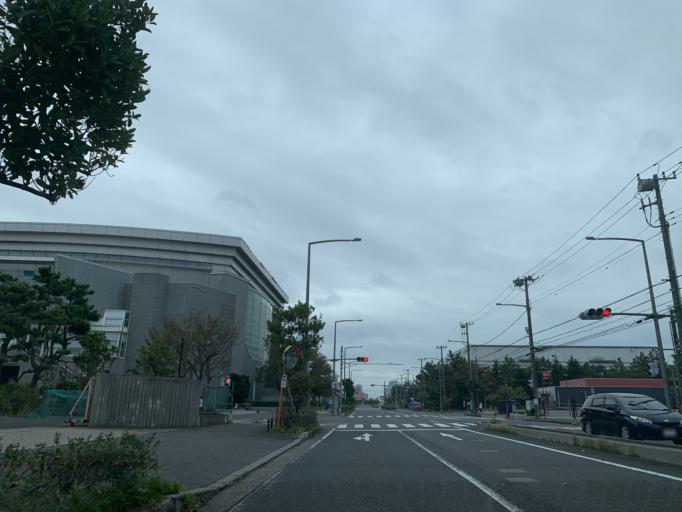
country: JP
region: Chiba
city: Funabashi
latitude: 35.6666
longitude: 140.0098
